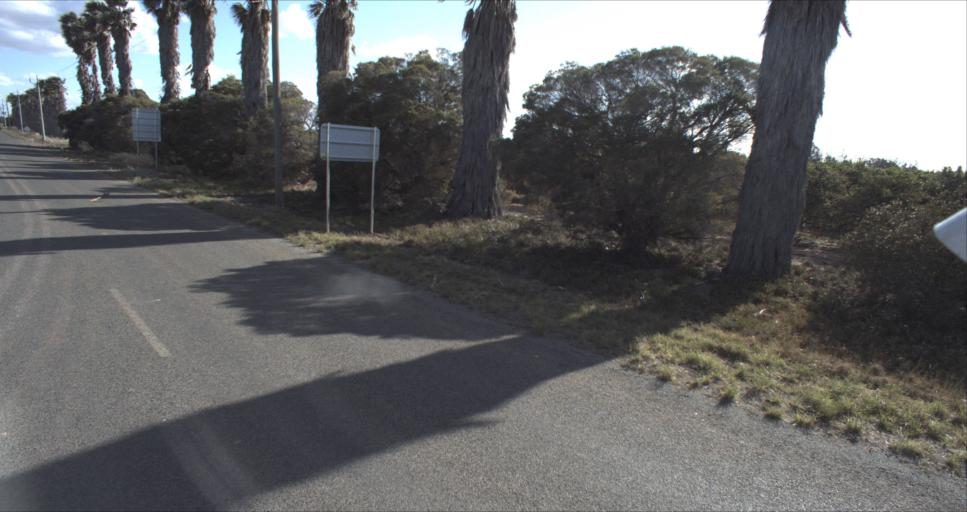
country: AU
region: New South Wales
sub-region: Leeton
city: Leeton
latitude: -34.5222
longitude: 146.2830
